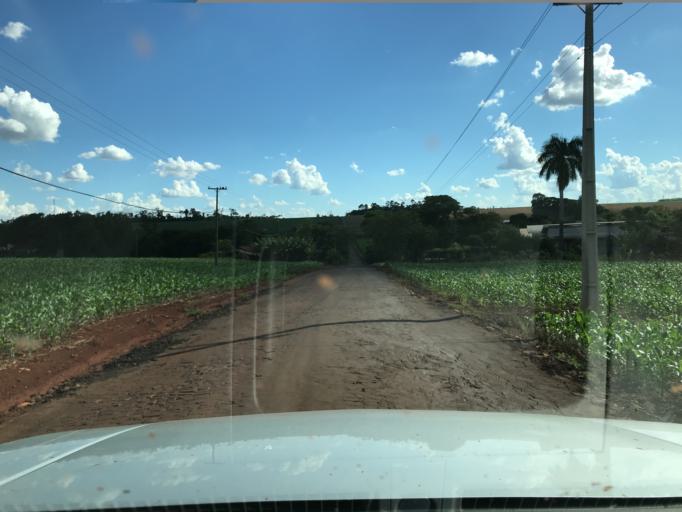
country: BR
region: Parana
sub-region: Palotina
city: Palotina
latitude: -24.2630
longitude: -53.8015
